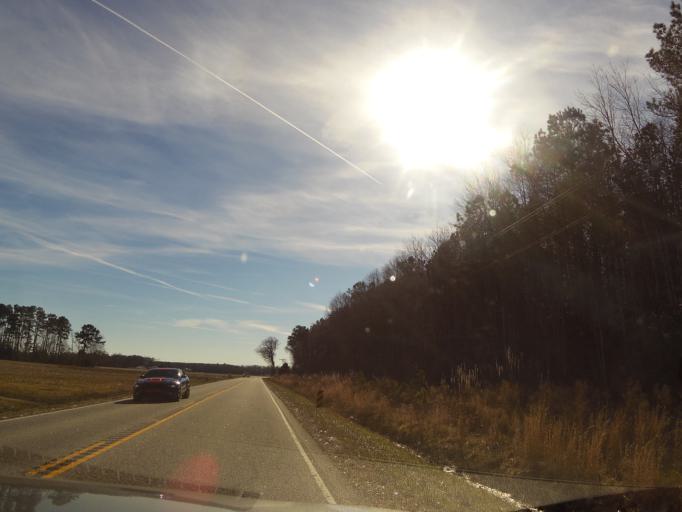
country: US
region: Virginia
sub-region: Isle of Wight County
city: Isle of Wight
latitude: 36.9331
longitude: -76.6871
